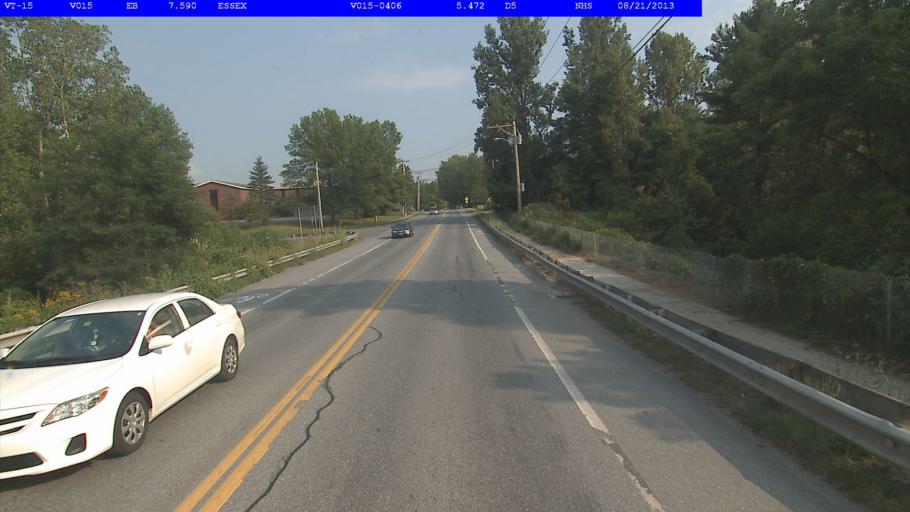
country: US
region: Vermont
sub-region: Chittenden County
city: Essex Junction
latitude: 44.5107
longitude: -73.0578
